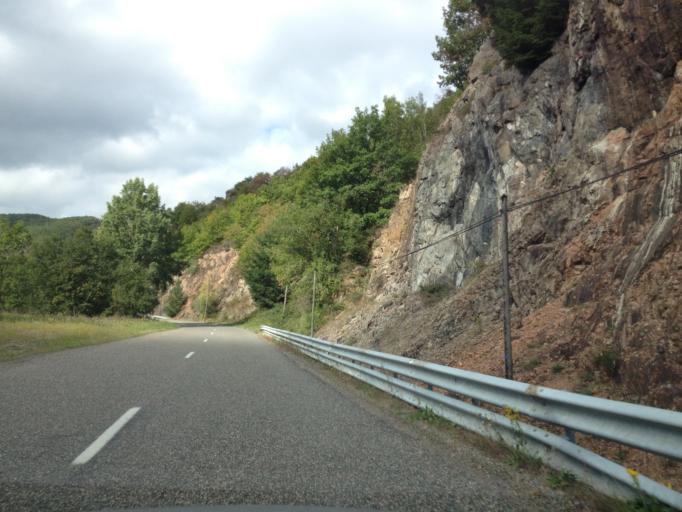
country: FR
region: Rhone-Alpes
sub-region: Departement de la Loire
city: Renaison
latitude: 46.0389
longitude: 3.8687
